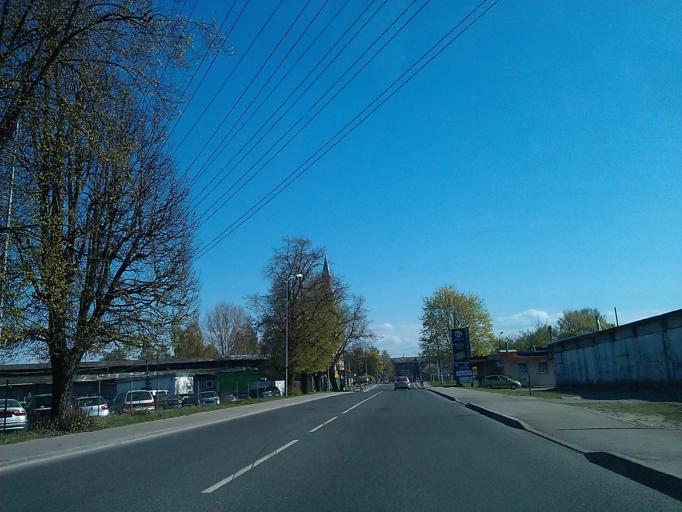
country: LV
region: Riga
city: Jaunciems
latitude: 56.9858
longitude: 24.1920
